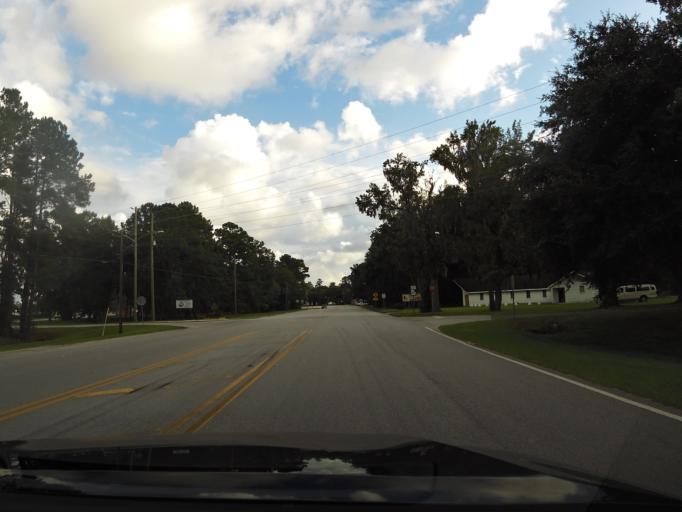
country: US
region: Georgia
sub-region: Liberty County
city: Midway
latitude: 31.7458
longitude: -81.4401
